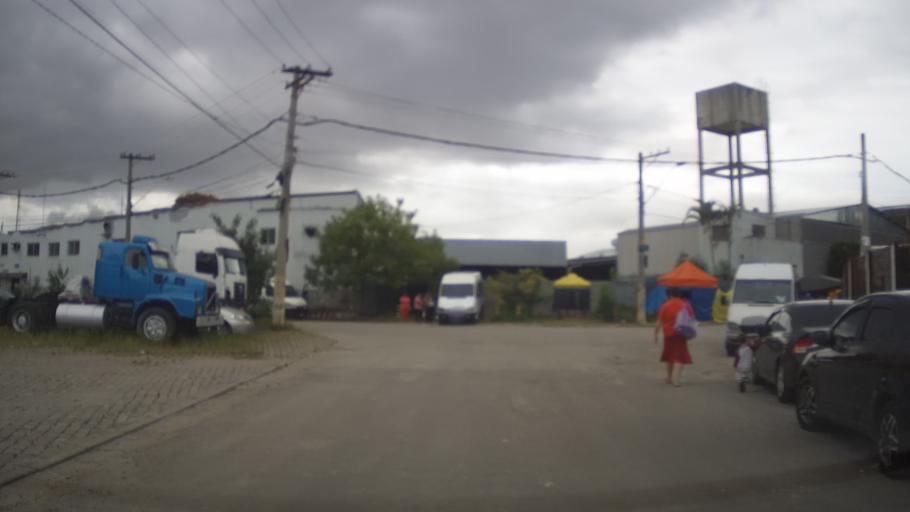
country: BR
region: Sao Paulo
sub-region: Guarulhos
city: Guarulhos
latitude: -23.4687
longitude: -46.4963
